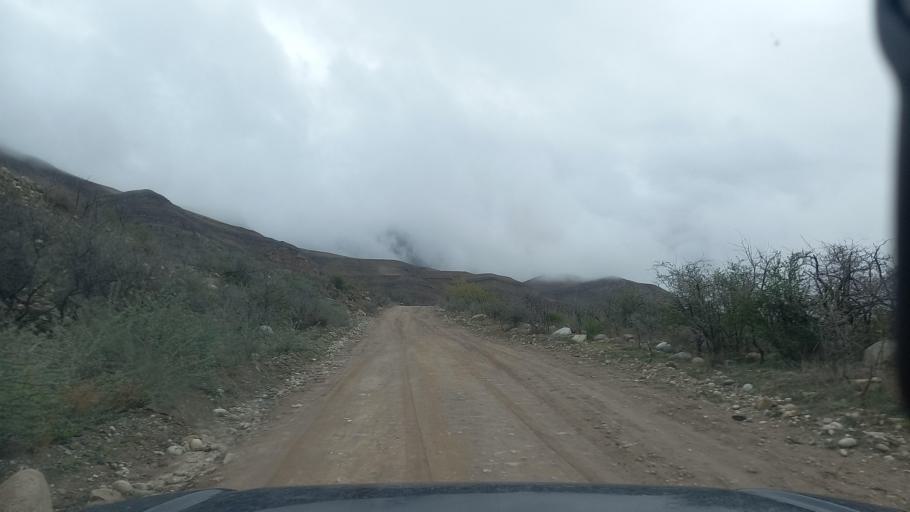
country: RU
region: Kabardino-Balkariya
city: Bylym
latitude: 43.4604
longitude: 43.0104
